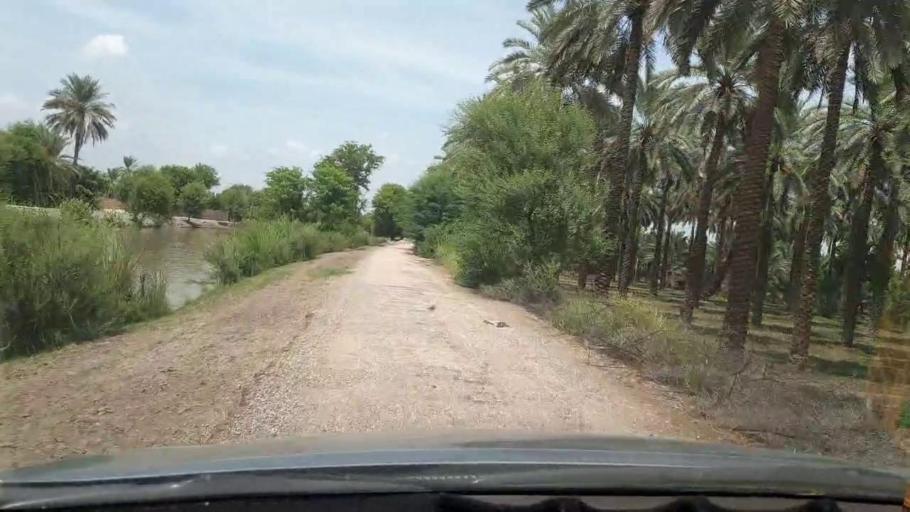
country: PK
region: Sindh
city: Khairpur
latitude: 27.4630
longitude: 68.8040
